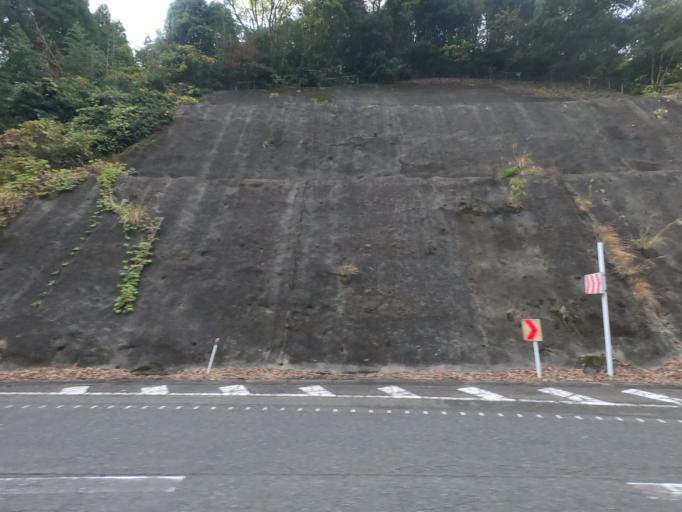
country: JP
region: Kumamoto
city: Minamata
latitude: 32.2451
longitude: 130.4854
